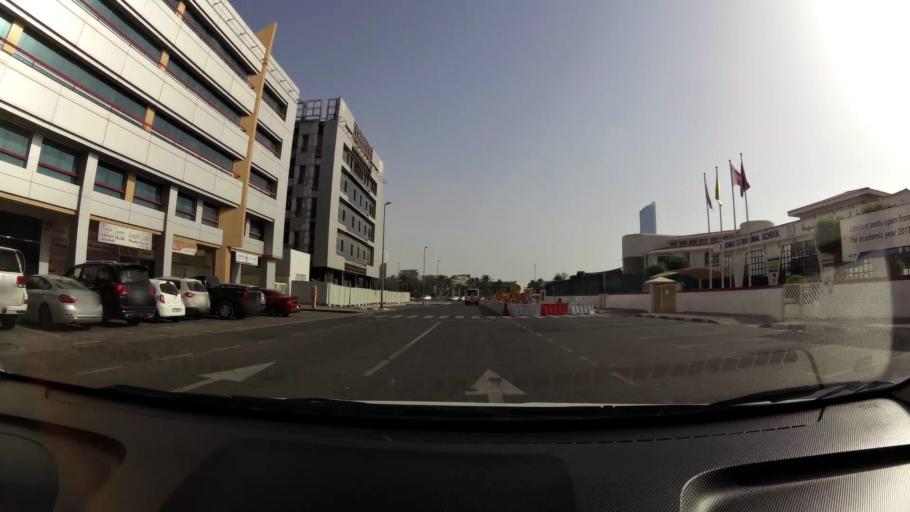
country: AE
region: Ash Shariqah
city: Sharjah
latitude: 25.2343
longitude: 55.3535
